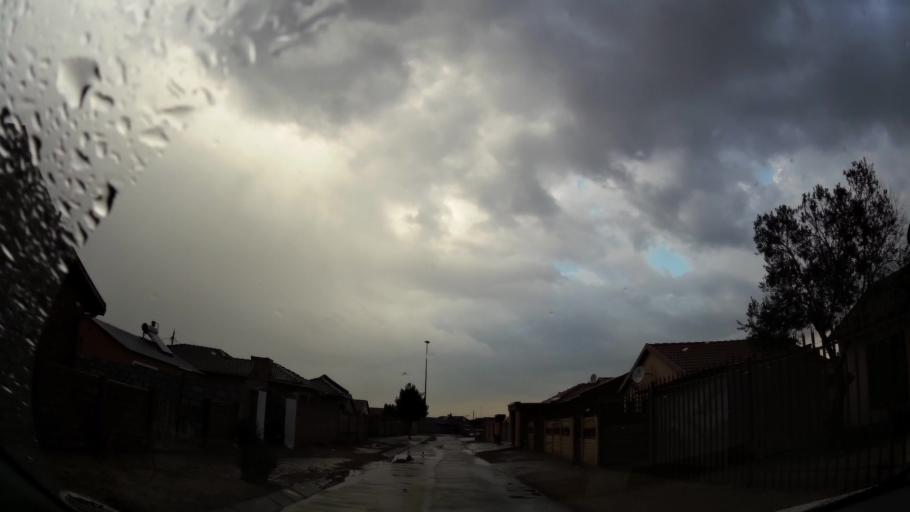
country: ZA
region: Gauteng
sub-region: Ekurhuleni Metropolitan Municipality
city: Germiston
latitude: -26.3625
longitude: 28.1300
